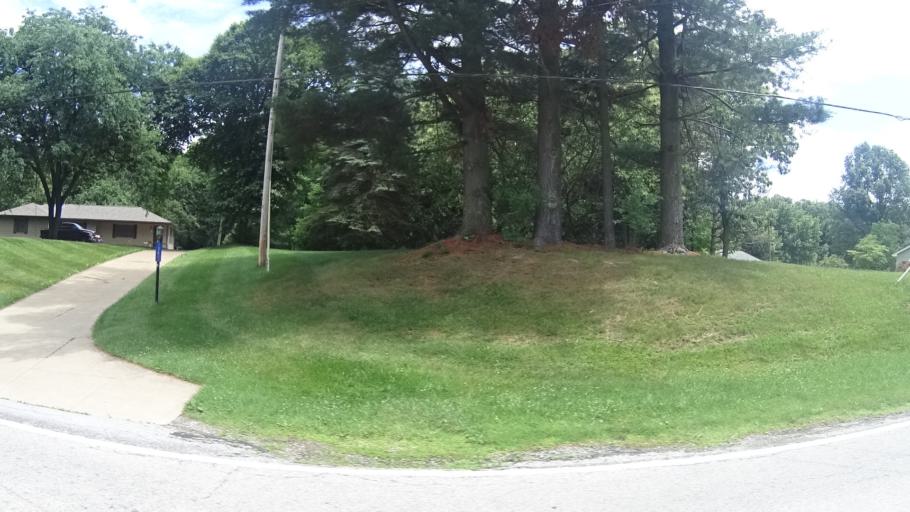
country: US
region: Ohio
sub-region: Erie County
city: Milan
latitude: 41.3038
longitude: -82.5864
